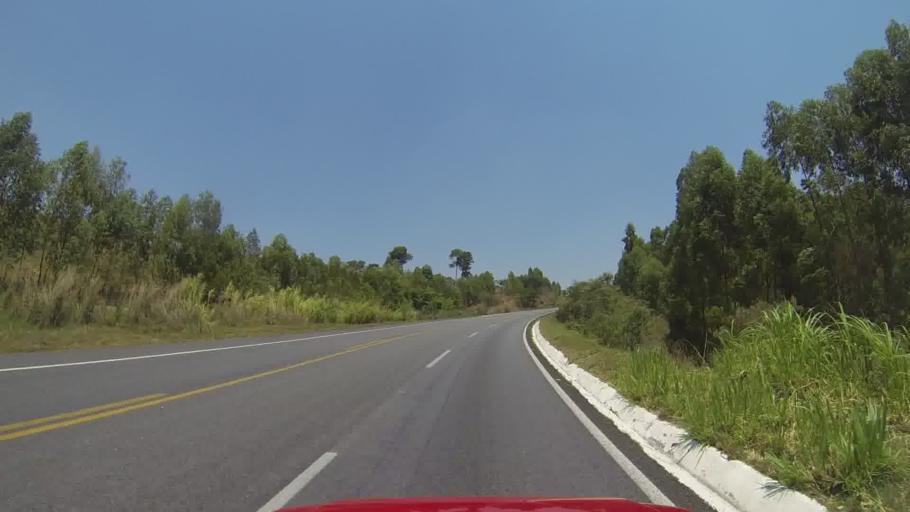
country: BR
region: Minas Gerais
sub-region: Itapecerica
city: Itapecerica
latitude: -20.2670
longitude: -45.1132
